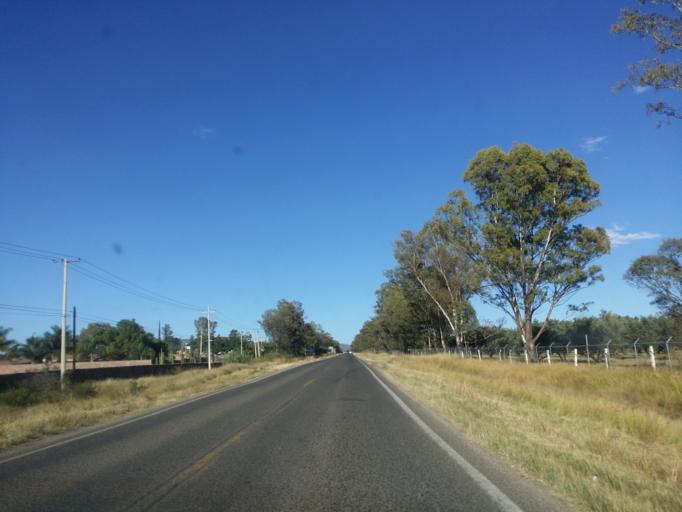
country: MX
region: Guanajuato
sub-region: Silao de la Victoria
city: El Refugio de los Sauces
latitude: 21.0289
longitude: -101.5328
